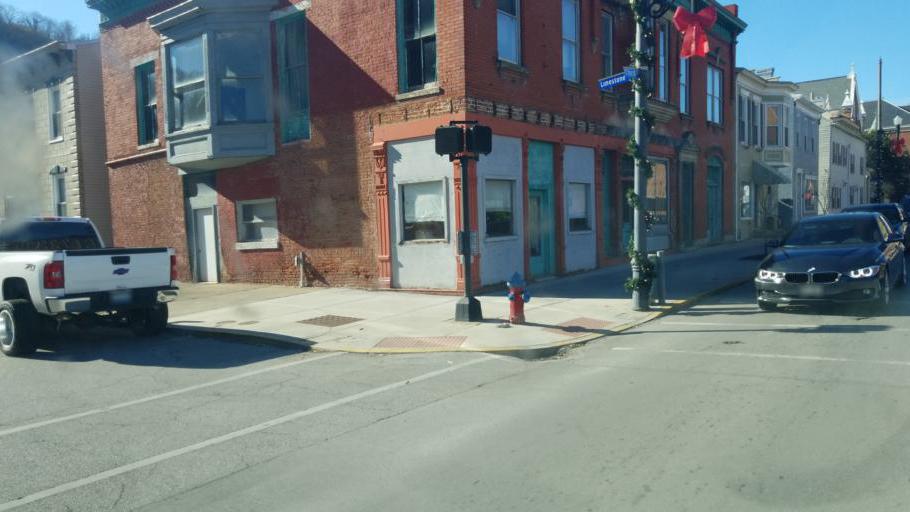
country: US
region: Ohio
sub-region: Brown County
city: Aberdeen
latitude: 38.6460
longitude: -83.7633
